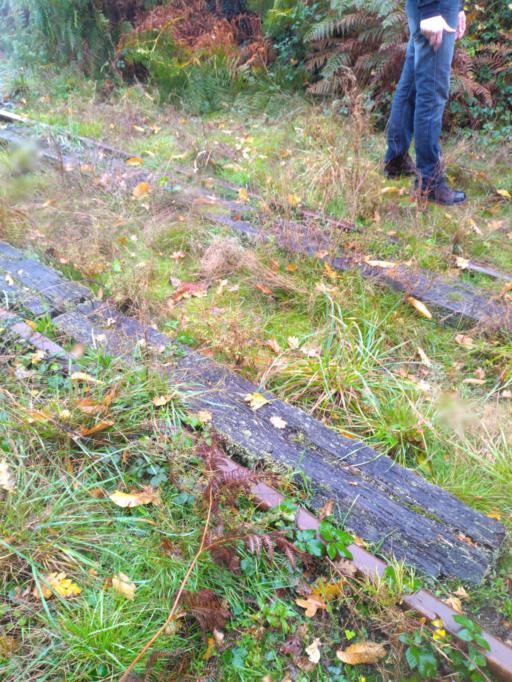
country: FR
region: Brittany
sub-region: Departement du Finistere
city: Rosporden
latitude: 47.9482
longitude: -3.8738
